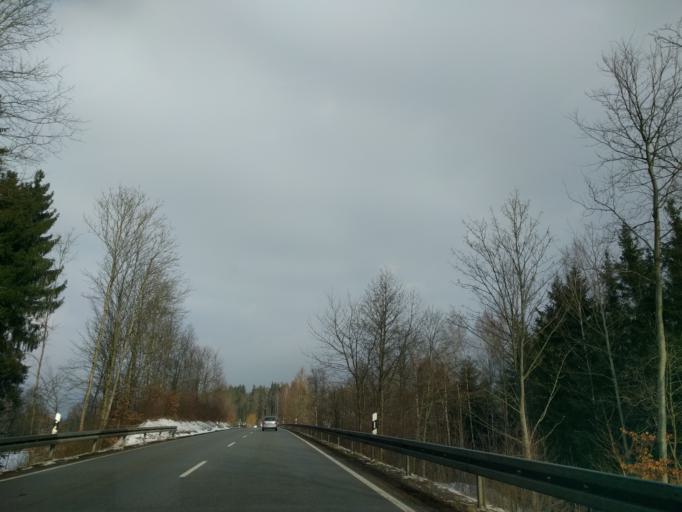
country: DE
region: Bavaria
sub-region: Lower Bavaria
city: Zwiesel
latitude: 49.0228
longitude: 13.2476
